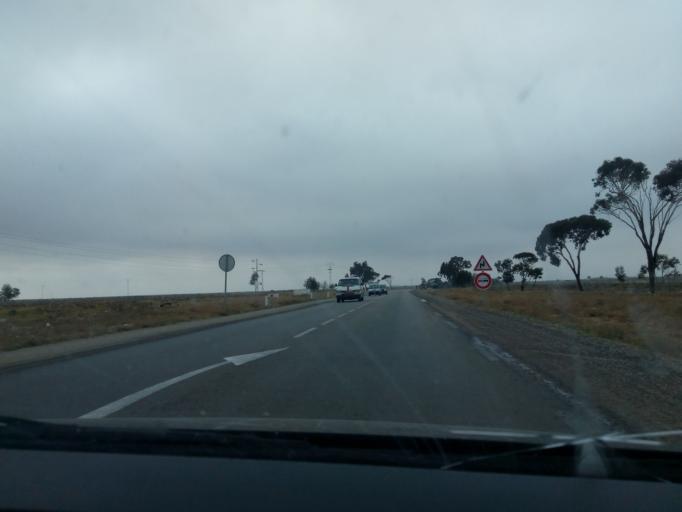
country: TN
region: Madanin
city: Medenine
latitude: 33.2734
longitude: 10.4684
